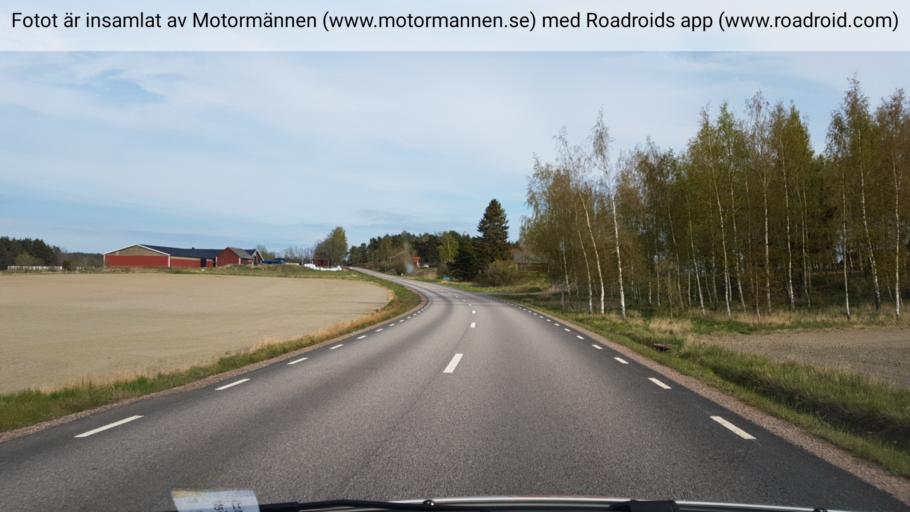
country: SE
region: Kalmar
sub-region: Vasterviks Kommun
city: Forserum
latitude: 57.9408
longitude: 16.4537
